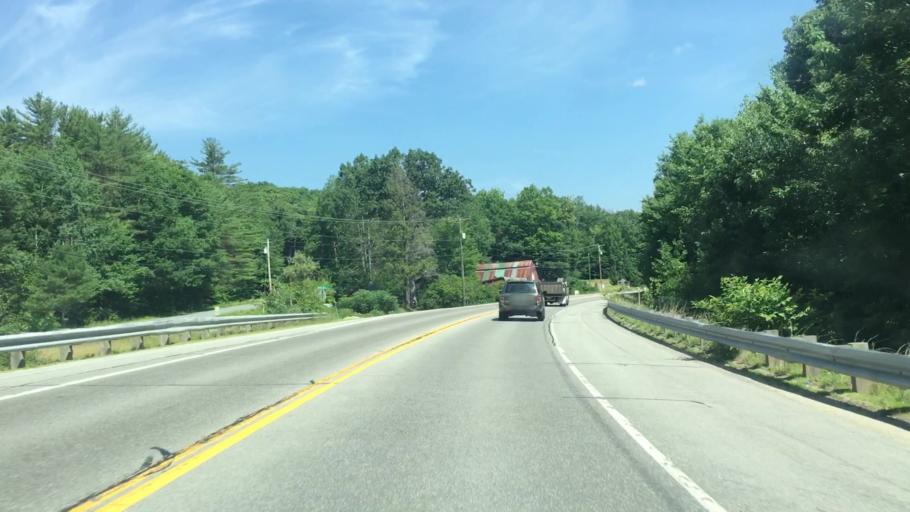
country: US
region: New Hampshire
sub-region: Merrimack County
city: Sutton
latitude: 43.2785
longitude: -71.9740
